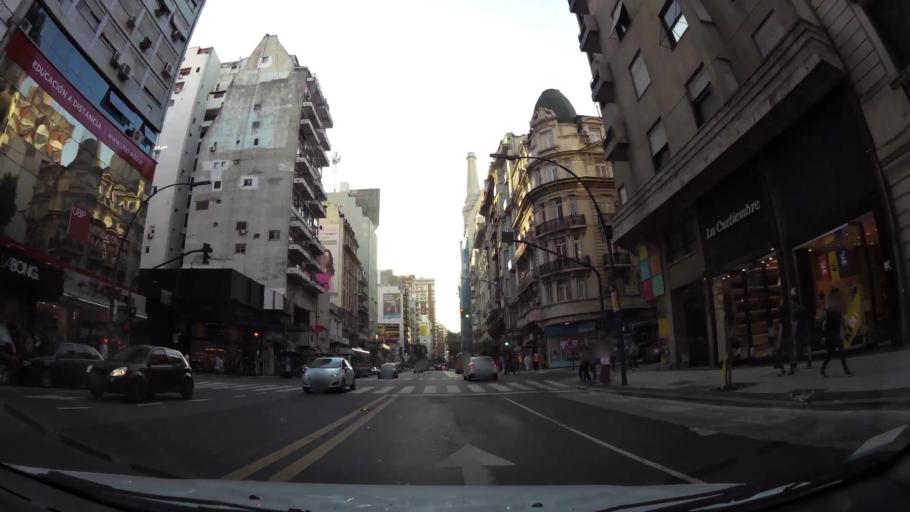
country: AR
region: Buenos Aires F.D.
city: Retiro
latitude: -34.5958
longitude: -58.3917
